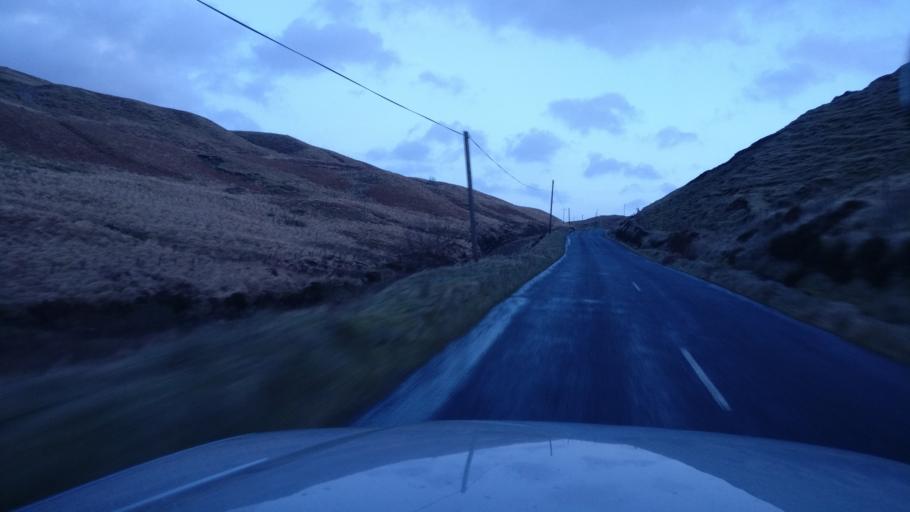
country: IE
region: Connaught
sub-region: Maigh Eo
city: Westport
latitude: 53.5893
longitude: -9.6876
